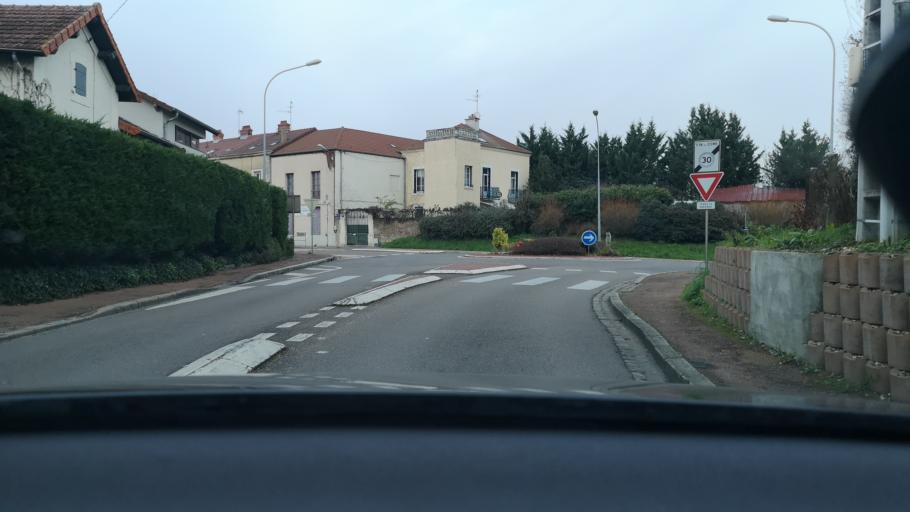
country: FR
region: Bourgogne
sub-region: Departement de Saone-et-Loire
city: Chalon-sur-Saone
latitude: 46.7817
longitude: 4.8409
